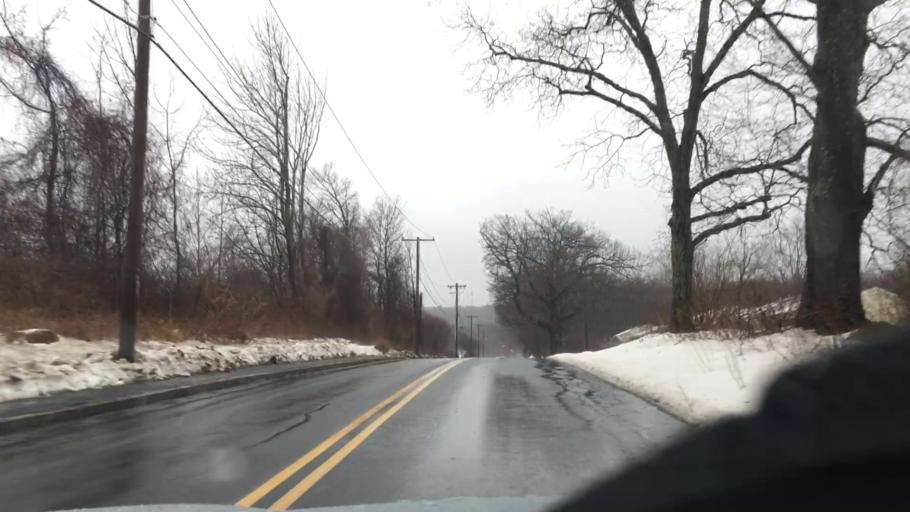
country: US
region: Massachusetts
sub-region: Hampshire County
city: Belchertown
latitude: 42.2883
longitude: -72.4124
